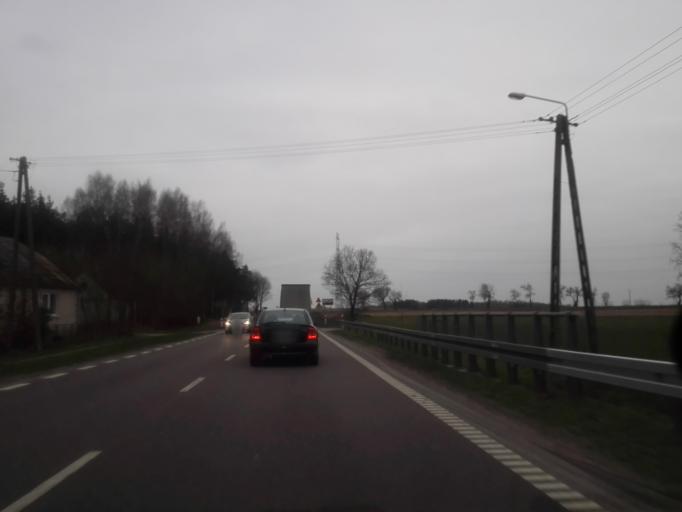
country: PL
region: Podlasie
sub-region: Powiat grajewski
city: Szczuczyn
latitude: 53.5921
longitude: 22.3401
